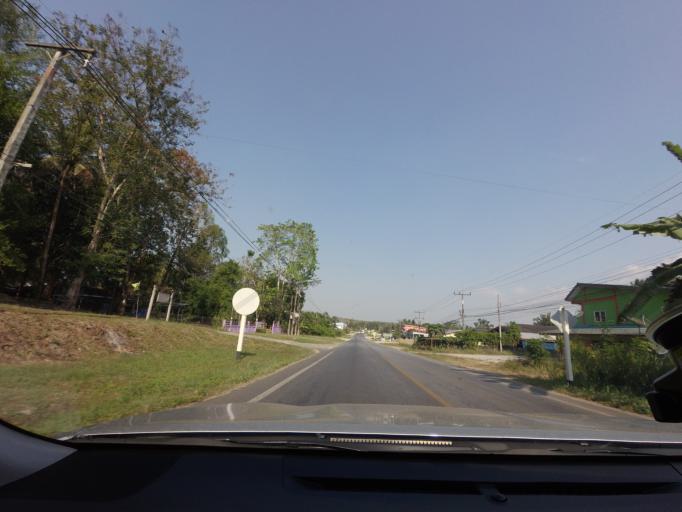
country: TH
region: Surat Thani
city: Phrasaeng
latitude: 8.5590
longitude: 99.1683
